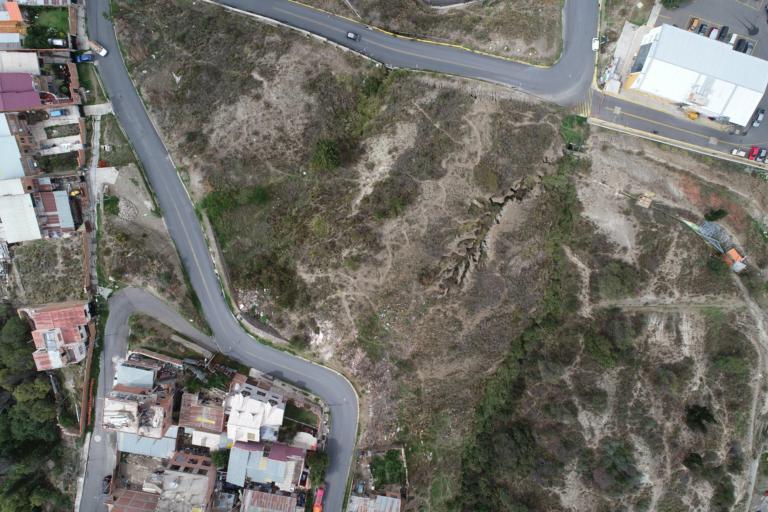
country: BO
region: La Paz
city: La Paz
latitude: -16.5156
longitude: -68.1094
